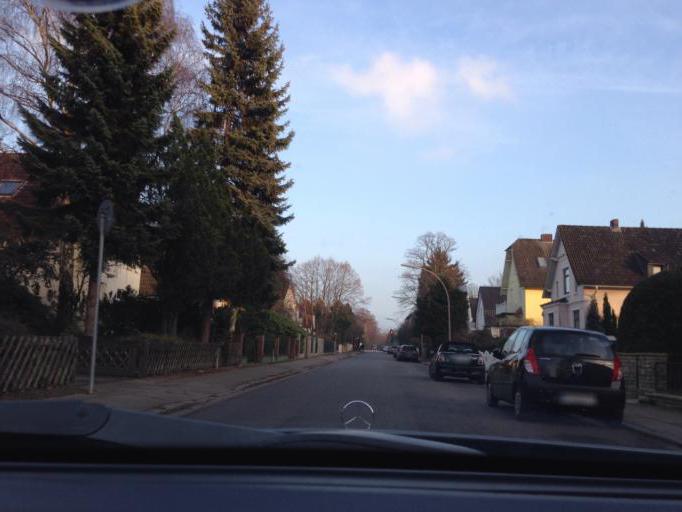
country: DE
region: Hamburg
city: Farmsen-Berne
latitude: 53.6090
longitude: 10.1479
